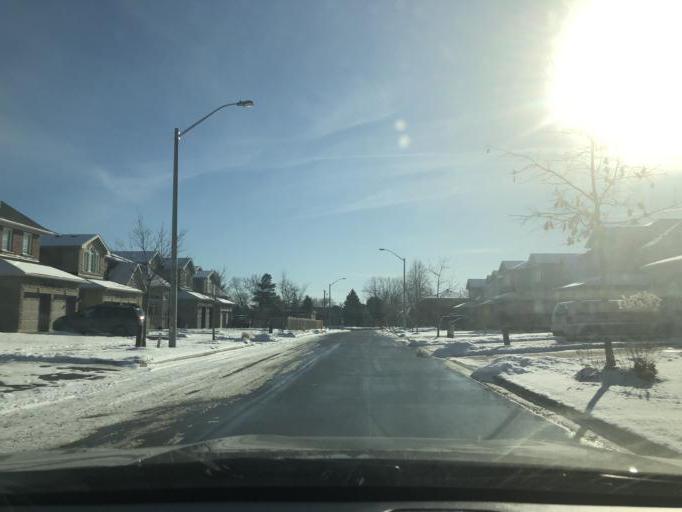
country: CA
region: Ontario
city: Scarborough
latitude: 43.7893
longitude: -79.1499
